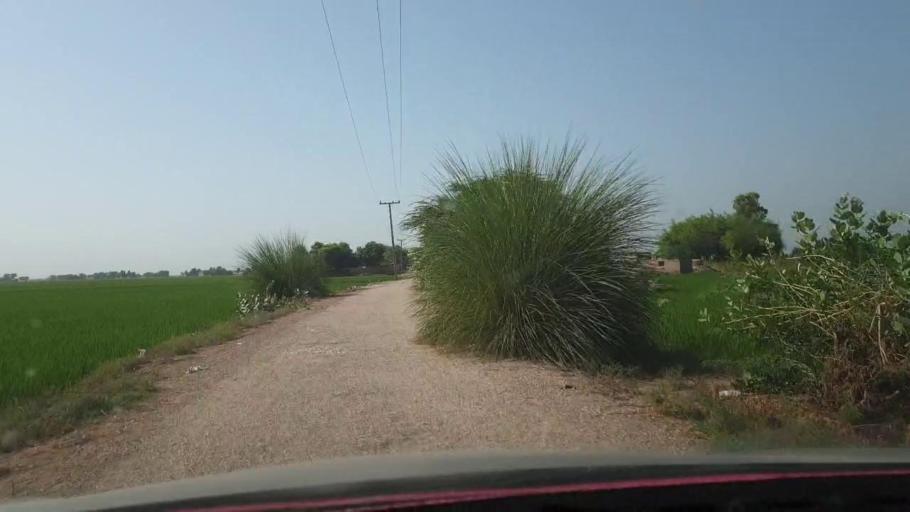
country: PK
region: Sindh
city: Nasirabad
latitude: 27.3794
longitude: 67.8829
